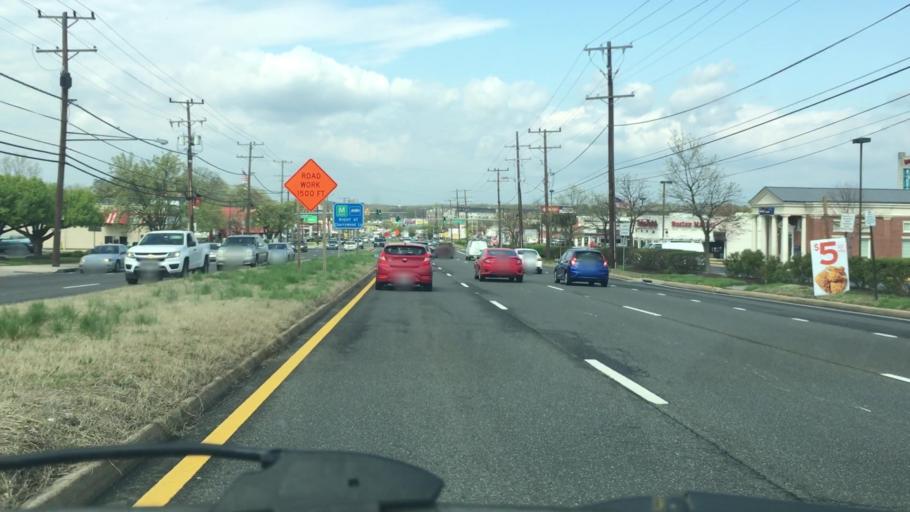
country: US
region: Maryland
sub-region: Prince George's County
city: Berwyn Heights
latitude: 38.9973
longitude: -76.9079
